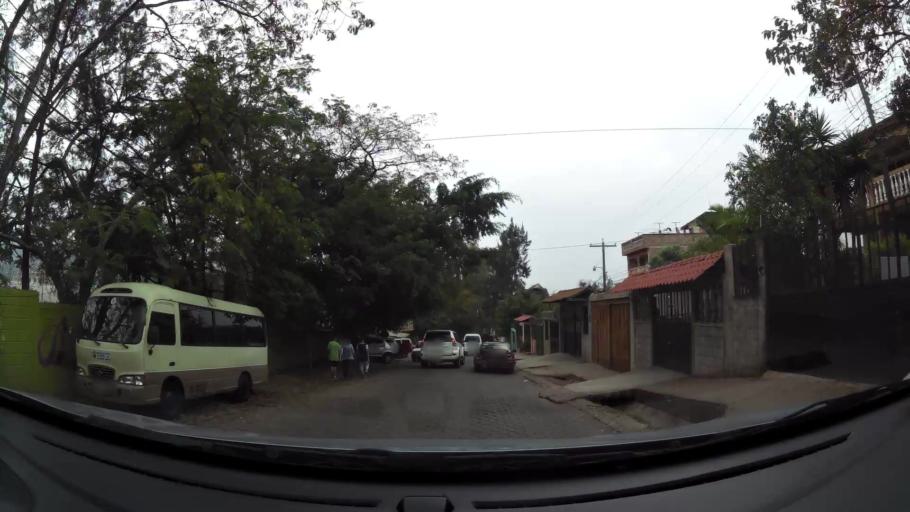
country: HN
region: Francisco Morazan
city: Tegucigalpa
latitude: 14.0728
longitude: -87.1742
